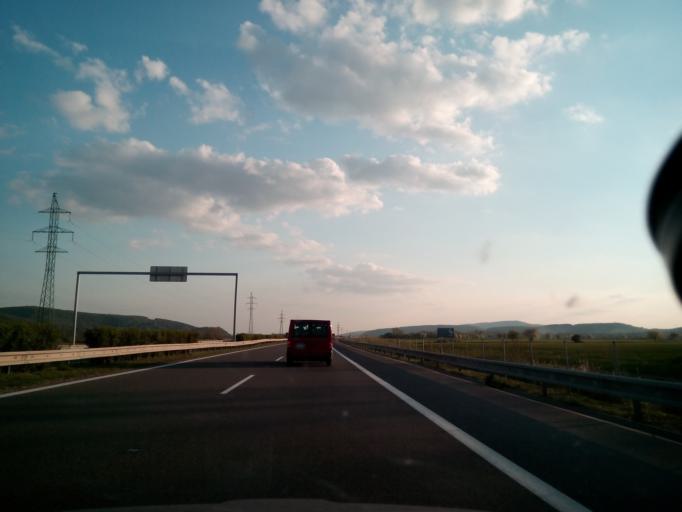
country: SK
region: Trenciansky
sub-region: Okres Trencin
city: Trencin
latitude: 48.8407
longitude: 17.9395
